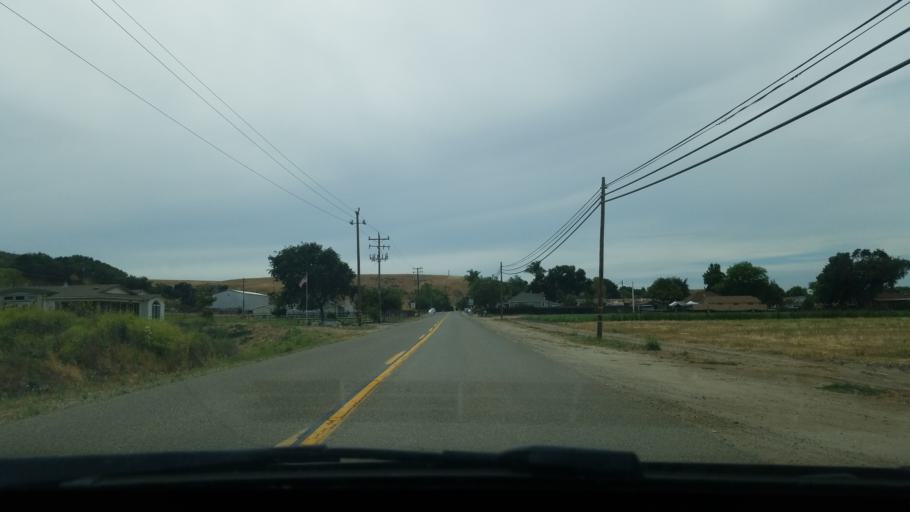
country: US
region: California
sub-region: Santa Barbara County
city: Los Alamos
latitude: 34.8645
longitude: -120.2887
